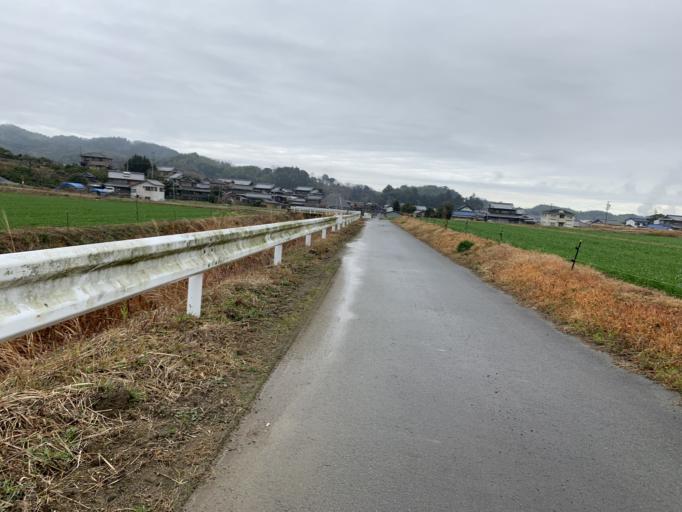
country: JP
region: Mie
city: Ise
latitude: 34.4756
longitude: 136.5465
